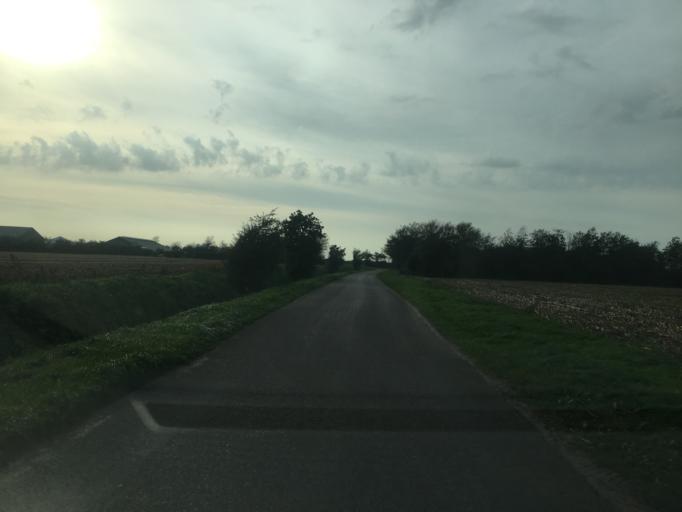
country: DE
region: Schleswig-Holstein
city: Bramstedtlund
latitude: 54.9140
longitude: 9.0688
